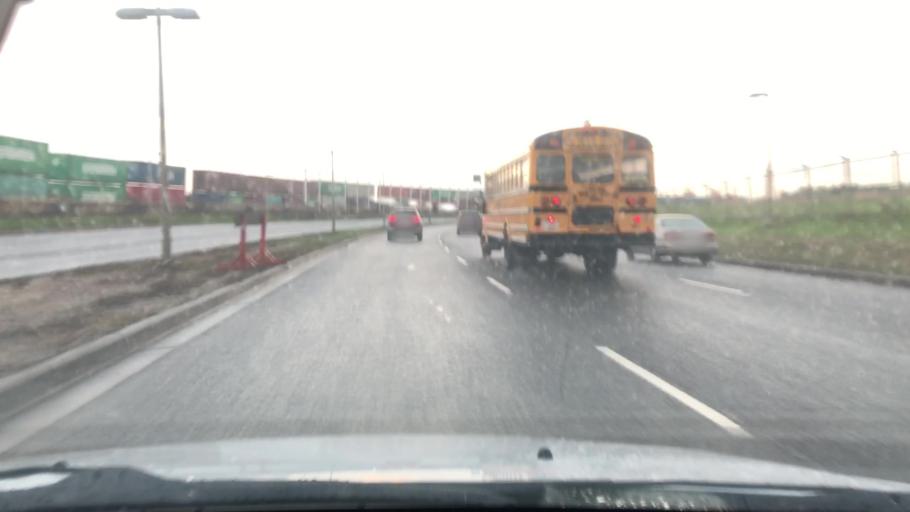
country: CA
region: Alberta
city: Edmonton
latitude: 53.5815
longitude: -113.5157
